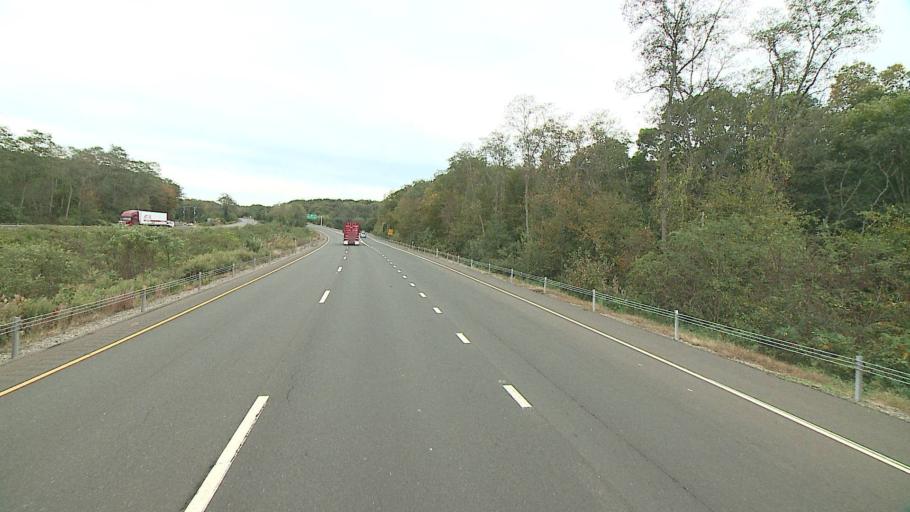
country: US
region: Connecticut
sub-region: Middlesex County
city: Essex Village
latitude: 41.3250
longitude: -72.3834
